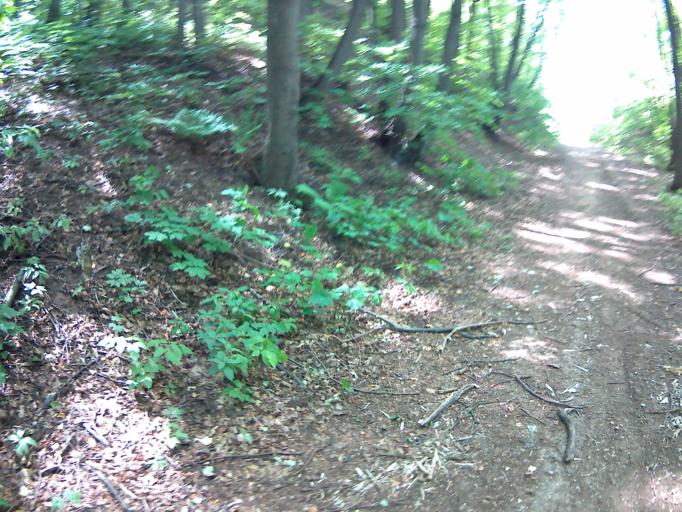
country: RU
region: Nizjnij Novgorod
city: Nizhniy Novgorod
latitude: 56.2389
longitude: 43.9382
